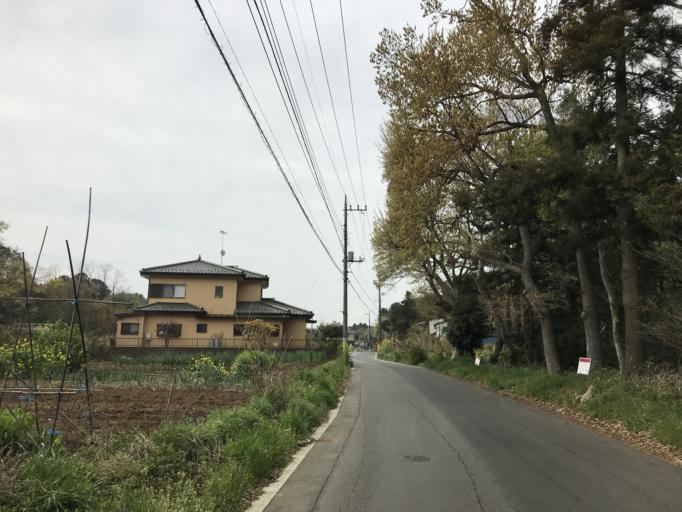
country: JP
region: Ibaraki
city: Moriya
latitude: 35.9462
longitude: 140.0091
